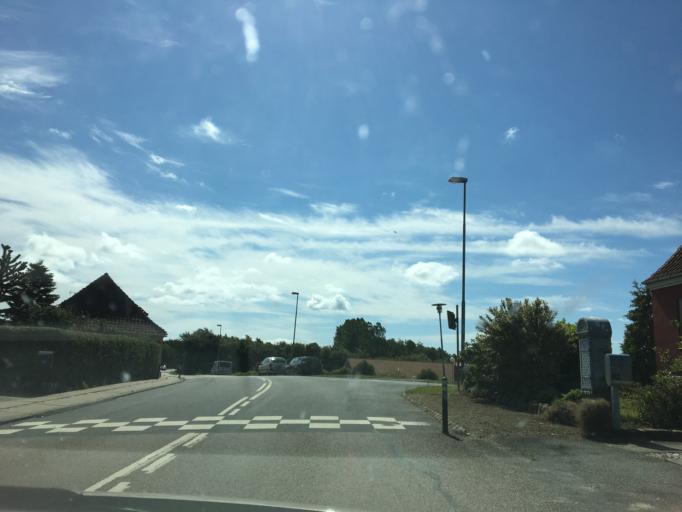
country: DK
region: South Denmark
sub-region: Langeland Kommune
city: Rudkobing
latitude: 54.9310
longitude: 10.7260
